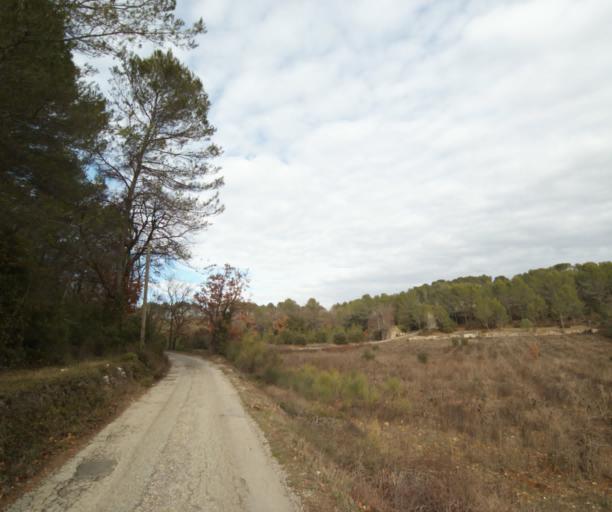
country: FR
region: Provence-Alpes-Cote d'Azur
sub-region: Departement du Var
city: Trans-en-Provence
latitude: 43.5118
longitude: 6.4967
